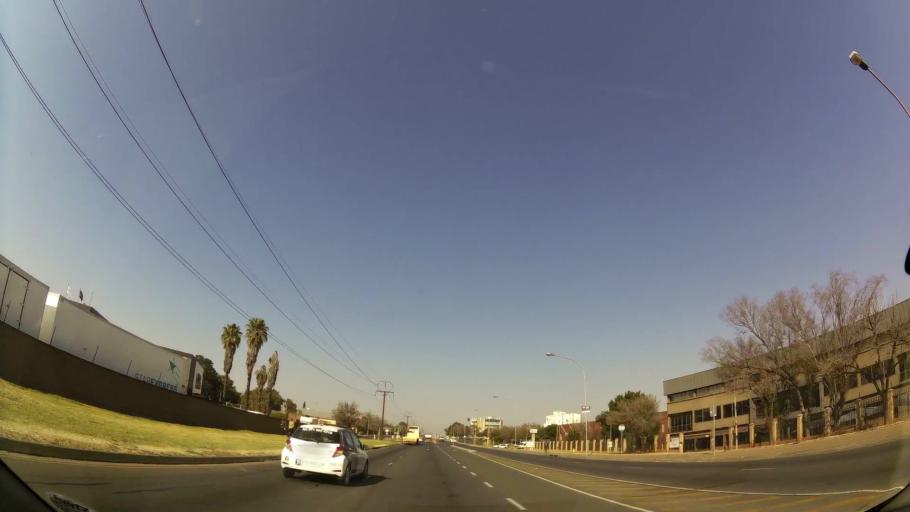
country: ZA
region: Gauteng
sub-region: City of Johannesburg Metropolitan Municipality
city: Modderfontein
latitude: -26.1355
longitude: 28.2020
